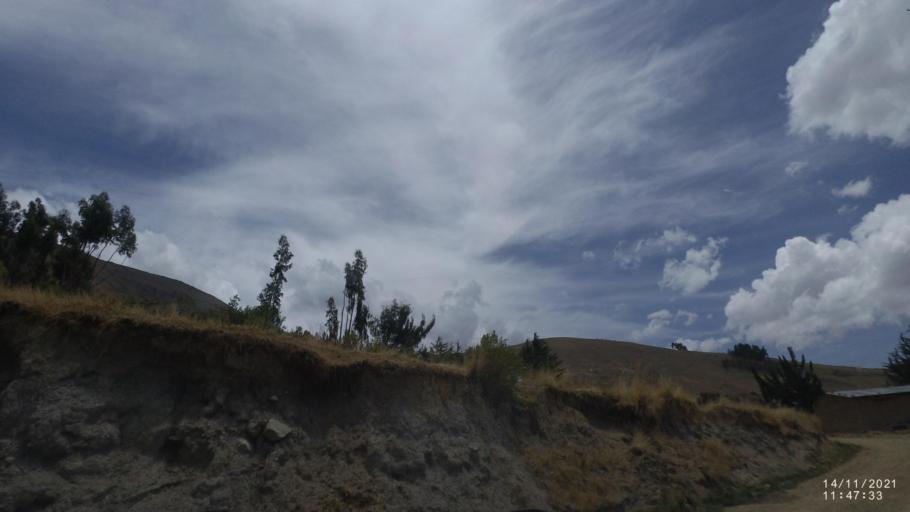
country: BO
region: Cochabamba
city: Colomi
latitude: -17.3531
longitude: -65.9851
